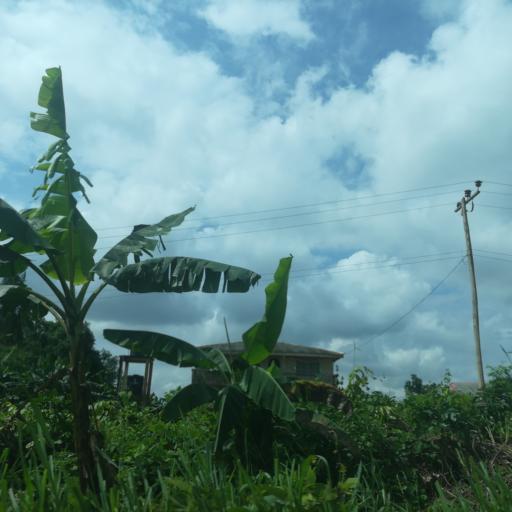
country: NG
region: Ogun
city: Odogbolu
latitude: 6.6520
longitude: 3.7027
